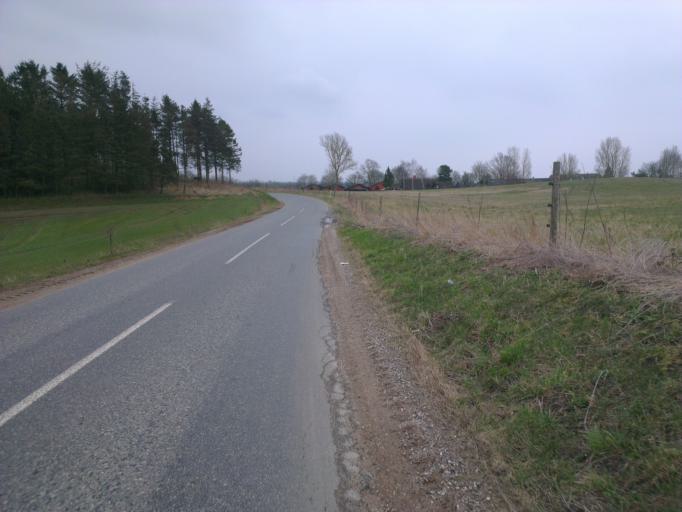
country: DK
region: Capital Region
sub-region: Egedal Kommune
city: Olstykke
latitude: 55.8340
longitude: 12.1286
